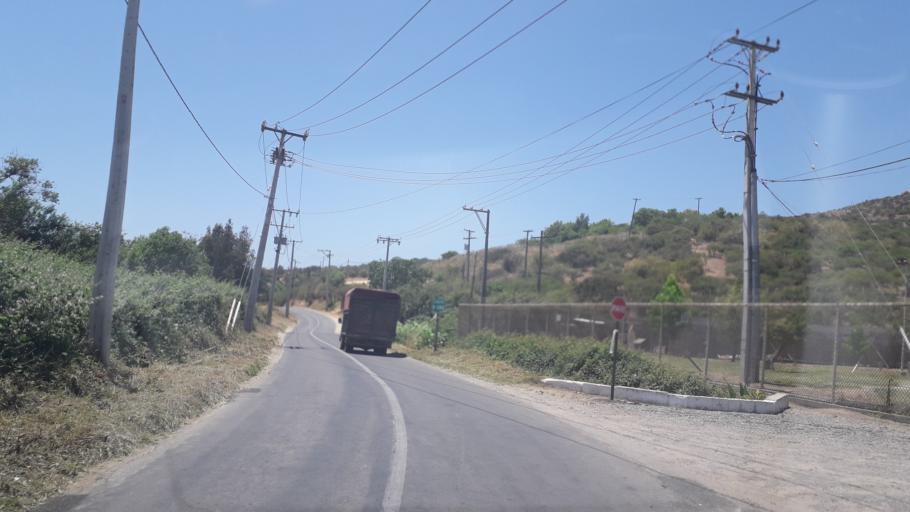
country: CL
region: Valparaiso
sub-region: Provincia de Quillota
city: Quillota
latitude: -32.9351
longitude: -71.2654
